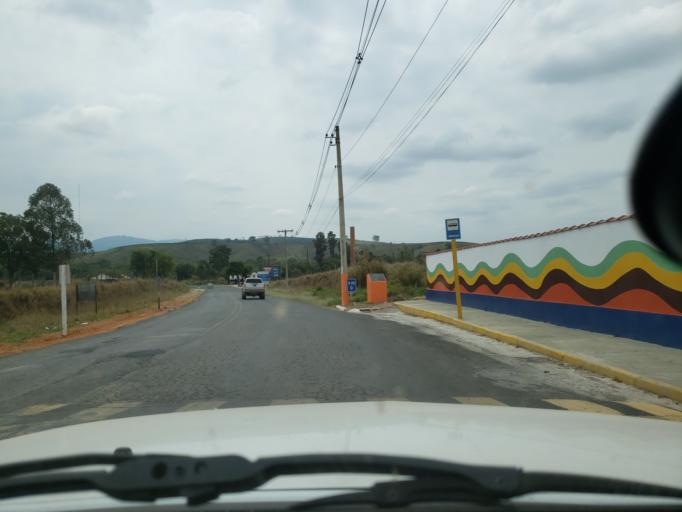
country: BR
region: Minas Gerais
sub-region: Jacutinga
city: Jacutinga
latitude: -22.2761
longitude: -46.6047
